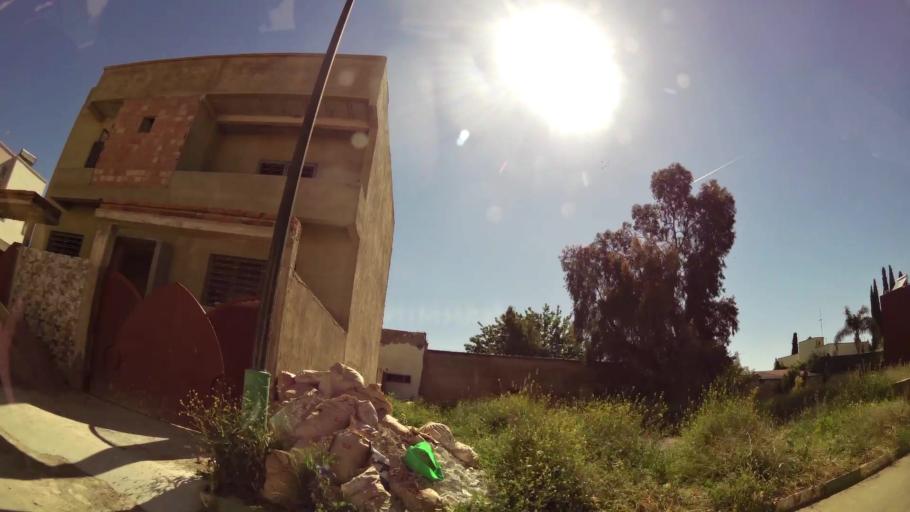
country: MA
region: Fes-Boulemane
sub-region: Fes
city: Fes
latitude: 34.0199
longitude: -4.9900
